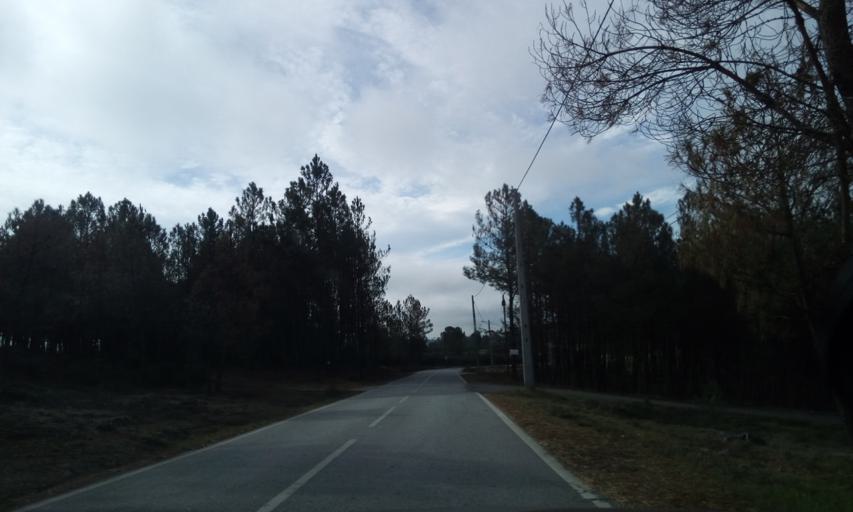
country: PT
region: Guarda
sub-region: Aguiar da Beira
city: Aguiar da Beira
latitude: 40.7772
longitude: -7.5183
